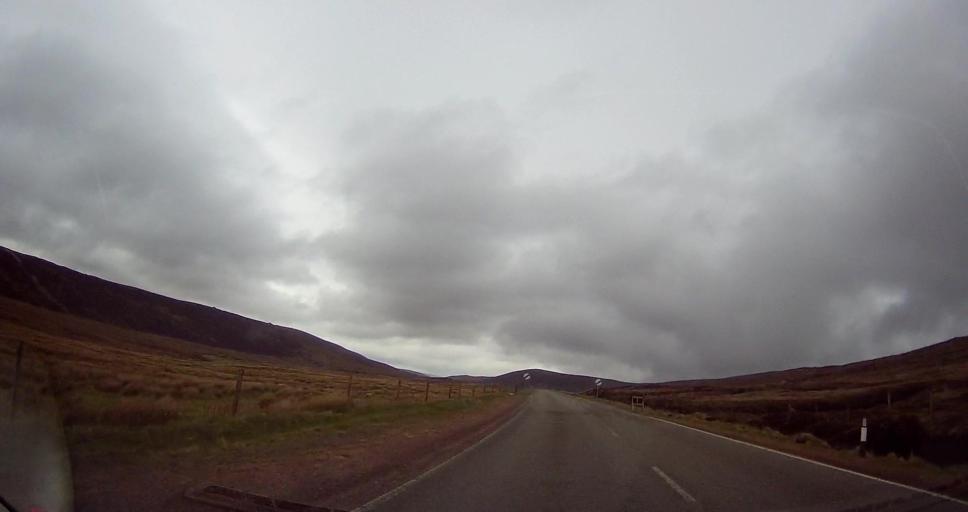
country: GB
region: Scotland
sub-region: Shetland Islands
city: Lerwick
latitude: 60.2808
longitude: -1.2443
